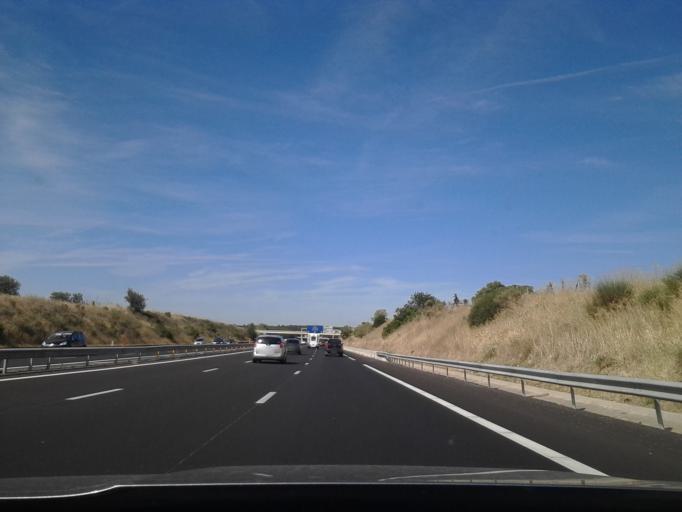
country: FR
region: Languedoc-Roussillon
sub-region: Departement de l'Herault
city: Poussan
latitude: 43.4843
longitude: 3.6935
